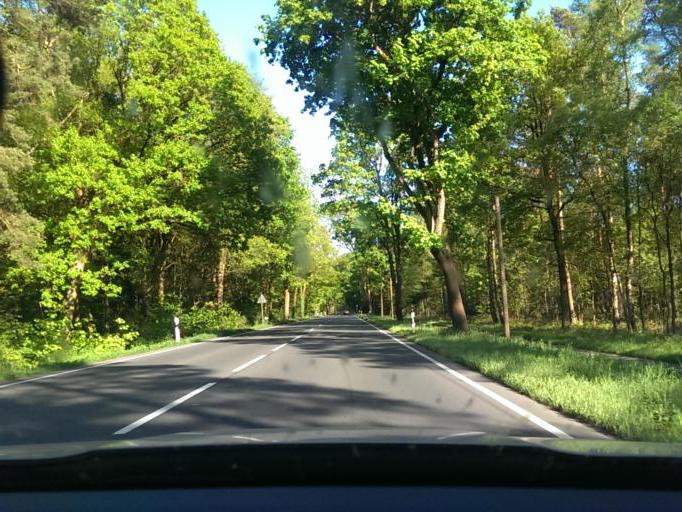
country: DE
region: Lower Saxony
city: Winsen (Aller)
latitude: 52.6373
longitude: 9.8883
